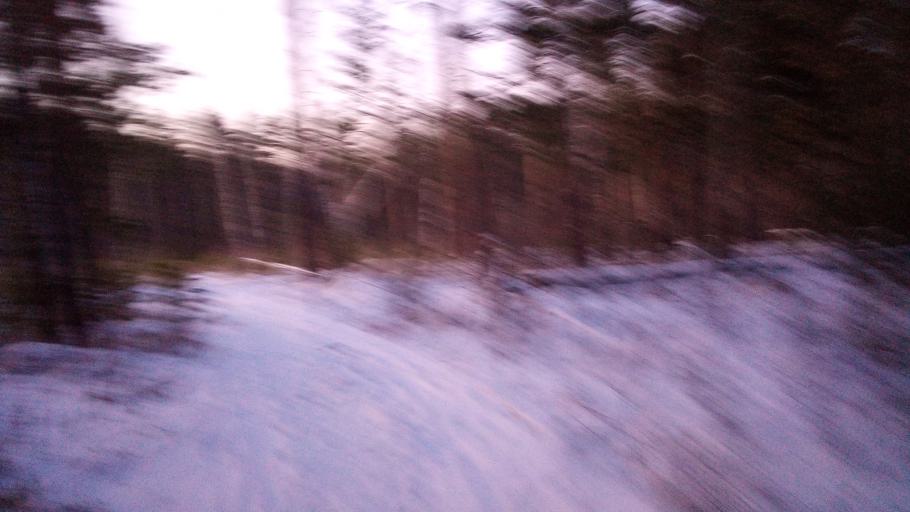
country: RU
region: Chelyabinsk
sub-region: Gorod Chelyabinsk
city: Chelyabinsk
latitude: 55.1646
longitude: 61.3316
